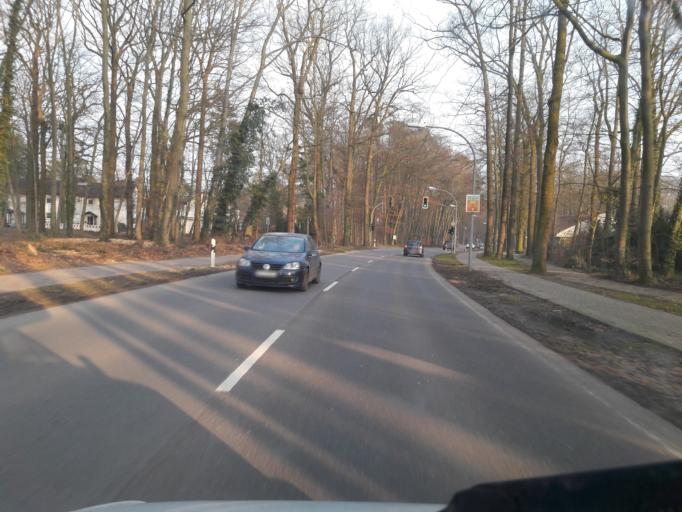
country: DE
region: North Rhine-Westphalia
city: Espelkamp
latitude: 52.3749
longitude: 8.6186
